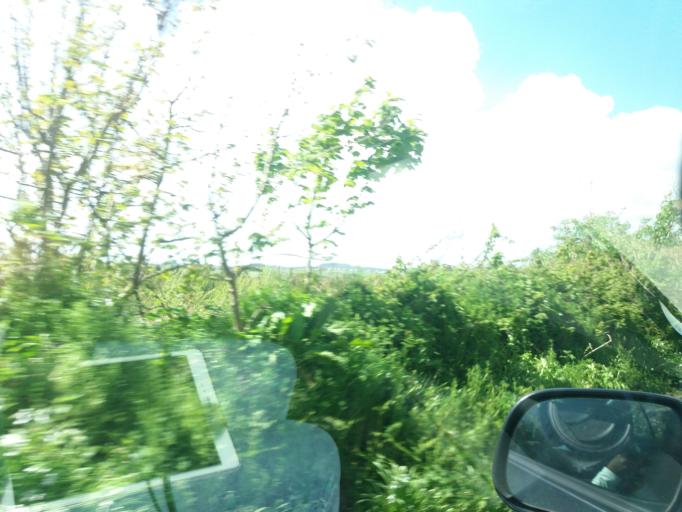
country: IE
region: Munster
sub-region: Waterford
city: Dunmore East
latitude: 52.2394
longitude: -6.9340
